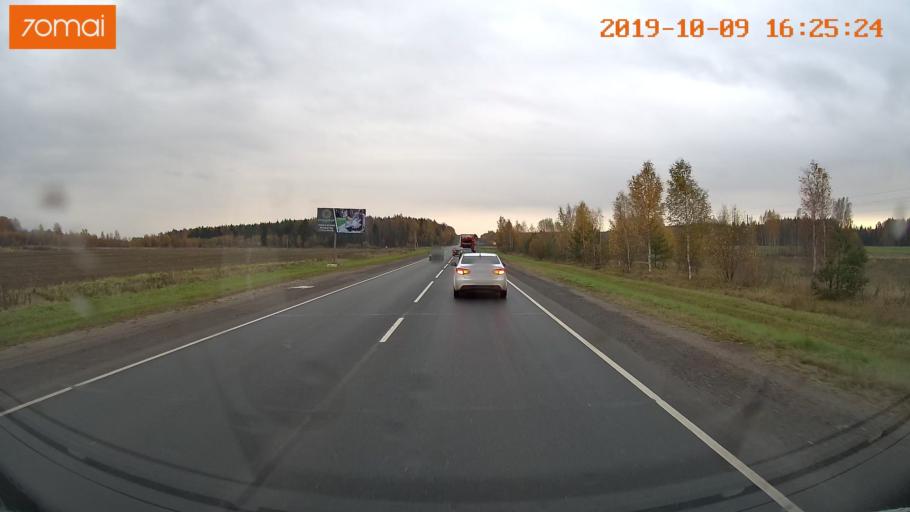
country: RU
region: Kostroma
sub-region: Kostromskoy Rayon
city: Kostroma
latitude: 57.6427
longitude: 40.9194
